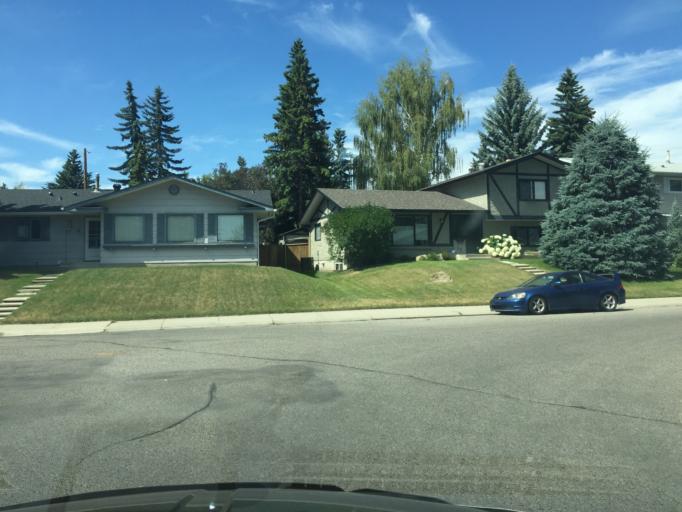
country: CA
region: Alberta
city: Calgary
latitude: 50.9464
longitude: -114.0535
